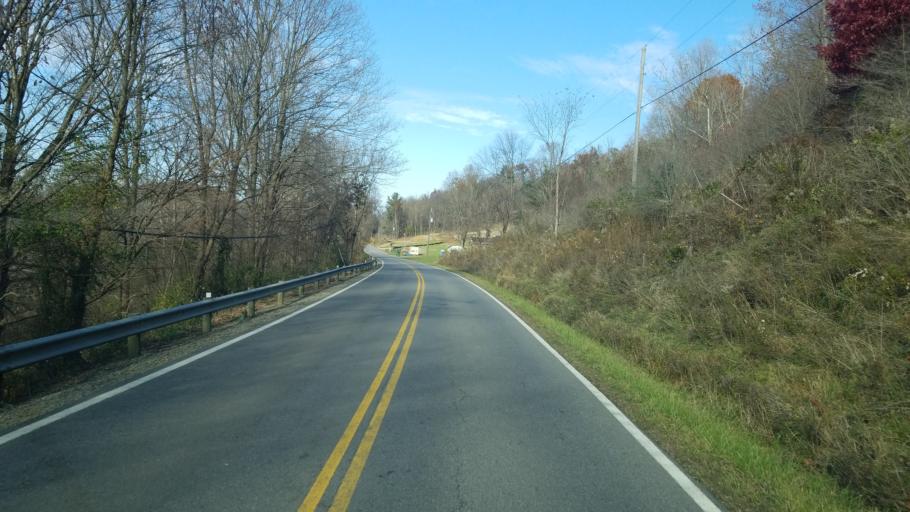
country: US
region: Ohio
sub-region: Licking County
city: Newark
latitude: 40.1356
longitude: -82.3435
